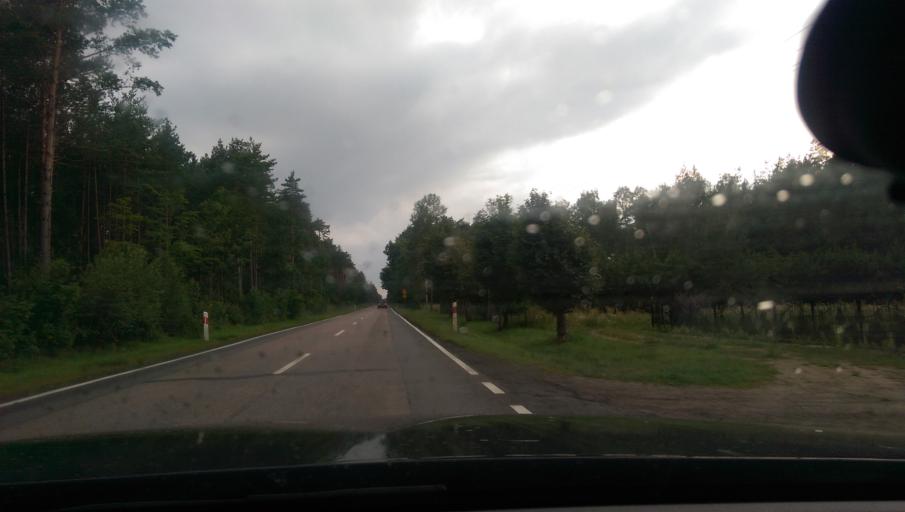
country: PL
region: Warmian-Masurian Voivodeship
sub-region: Powiat szczycienski
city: Szczytno
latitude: 53.5612
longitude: 21.0892
